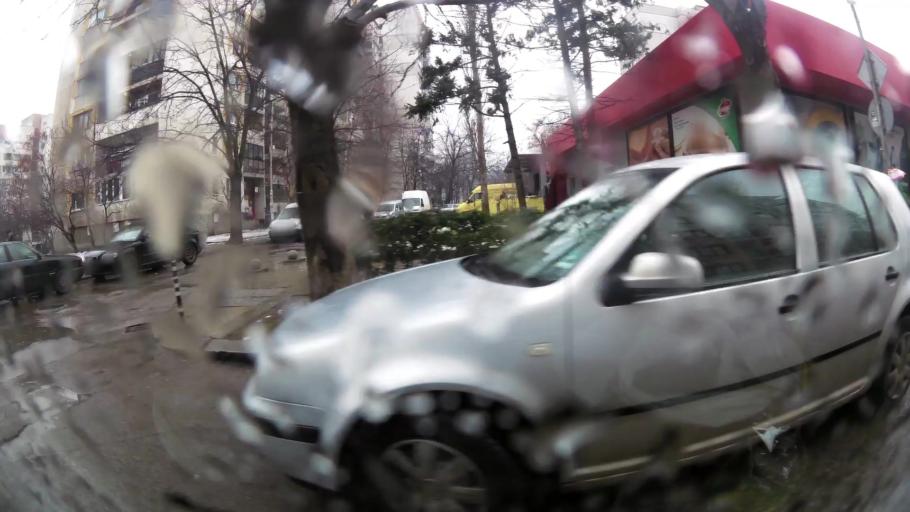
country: BG
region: Sofia-Capital
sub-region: Stolichna Obshtina
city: Sofia
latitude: 42.6719
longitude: 23.3001
